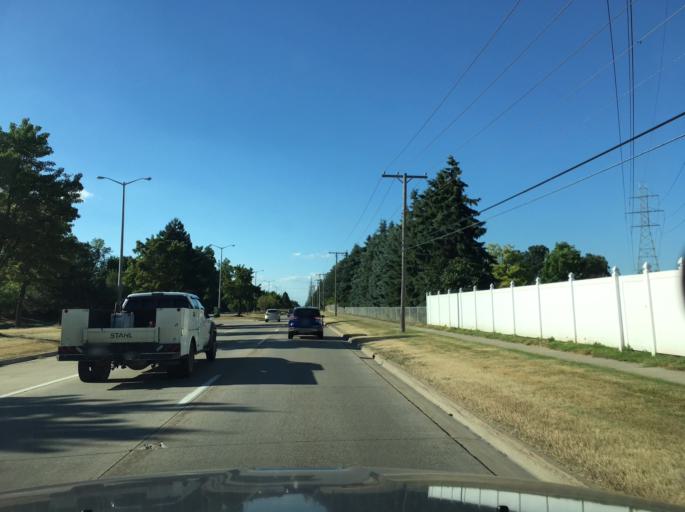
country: US
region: Michigan
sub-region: Macomb County
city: Sterling Heights
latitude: 42.5939
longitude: -82.9913
